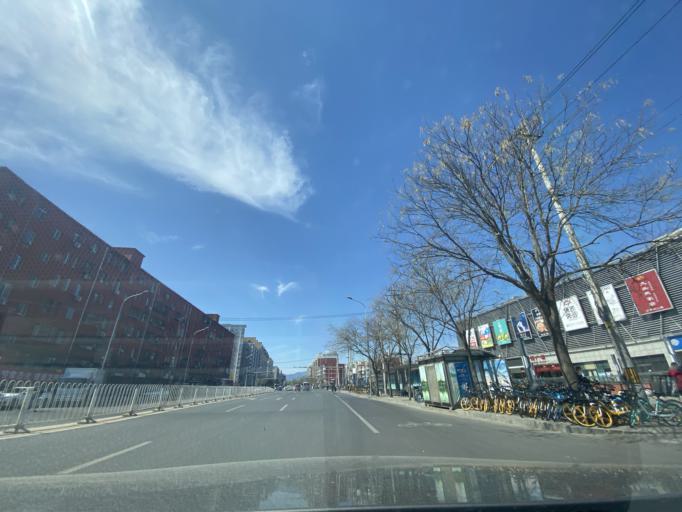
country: CN
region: Beijing
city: Sijiqing
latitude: 39.9283
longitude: 116.2486
